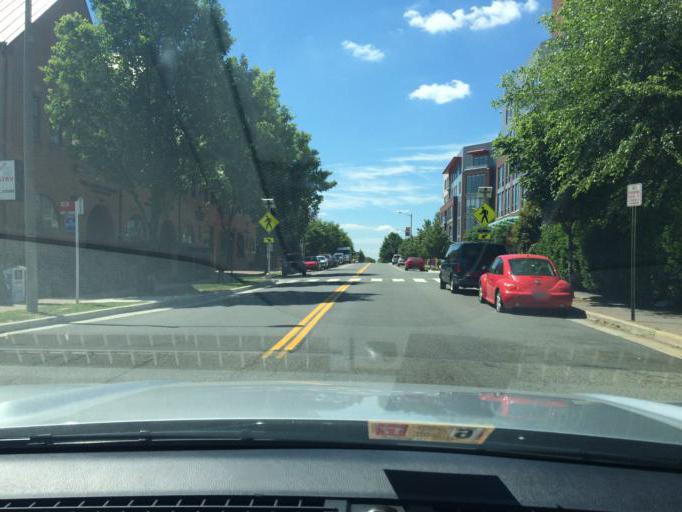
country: US
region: Virginia
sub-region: City of Alexandria
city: Alexandria
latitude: 38.8345
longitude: -77.0602
